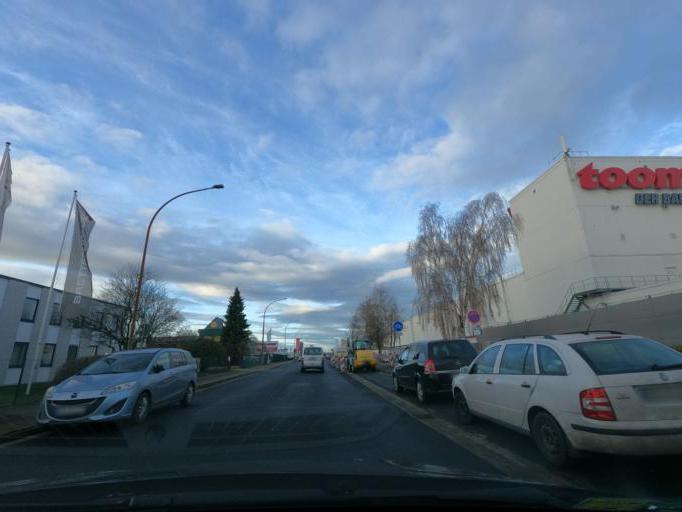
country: DE
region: Lower Saxony
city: Wolfenbuettel
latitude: 52.1586
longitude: 10.5068
